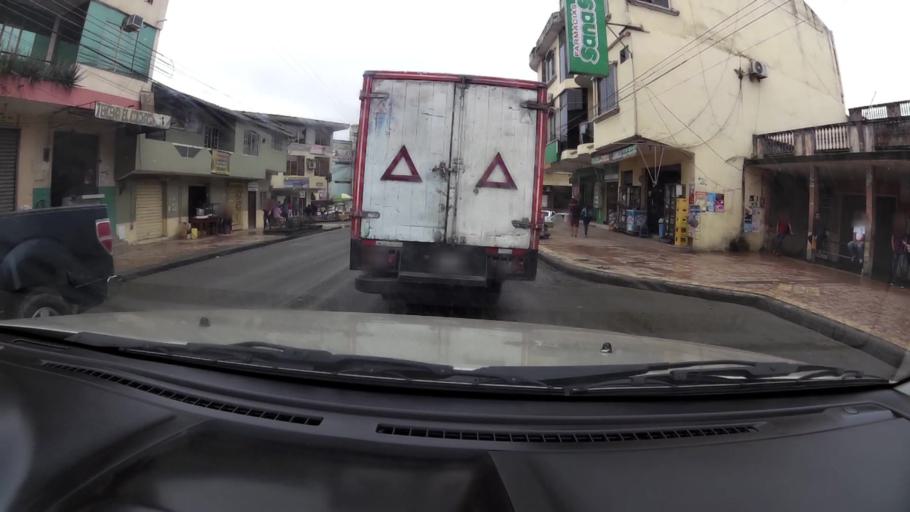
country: EC
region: Guayas
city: Balao
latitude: -3.0608
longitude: -79.7469
